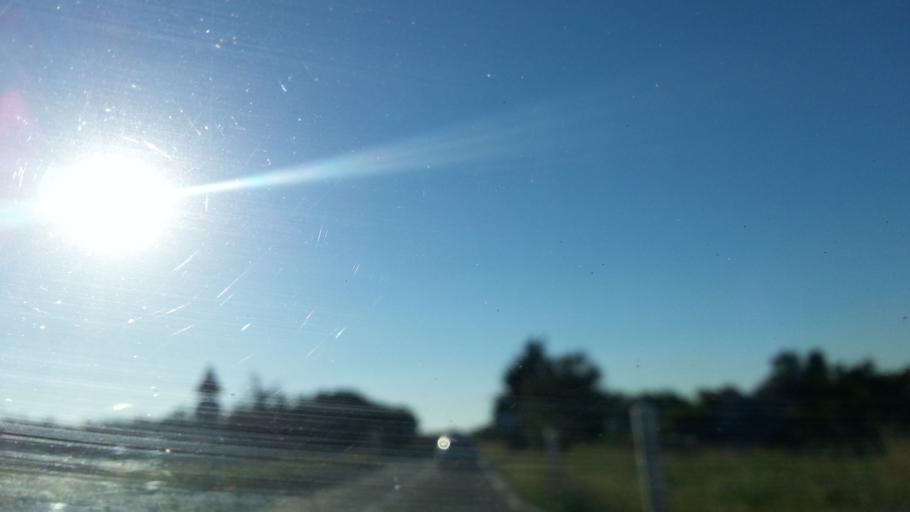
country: FR
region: Poitou-Charentes
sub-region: Departement de la Charente-Maritime
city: Dolus-d'Oleron
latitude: 45.9015
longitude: -1.2965
